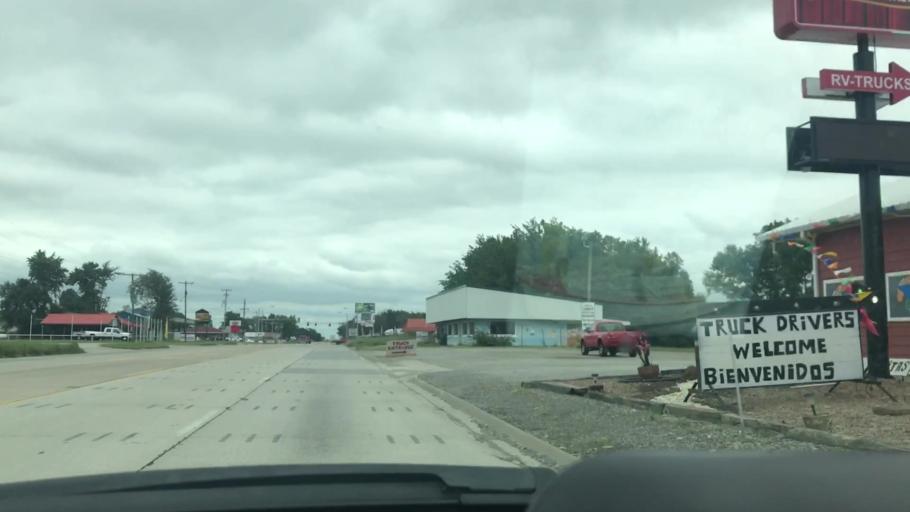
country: US
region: Oklahoma
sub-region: Mayes County
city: Pryor
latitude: 36.4344
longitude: -95.2726
